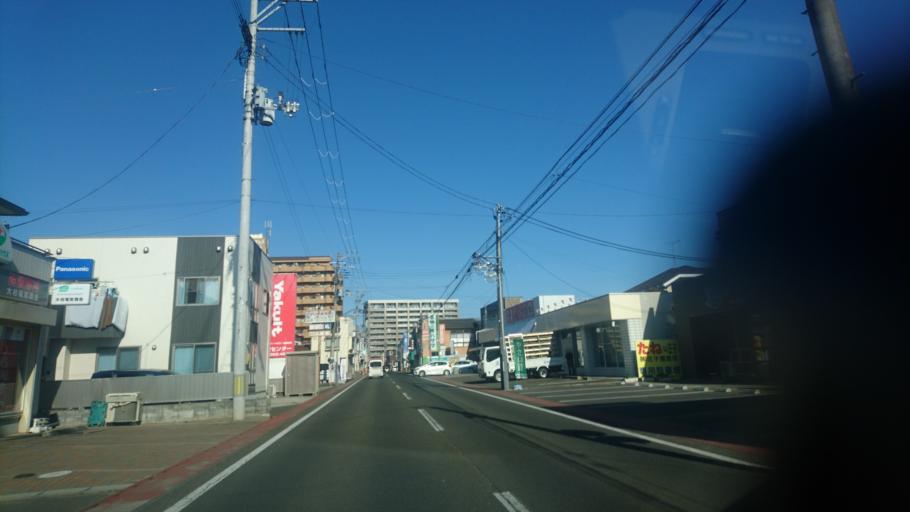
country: JP
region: Miyagi
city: Iwanuma
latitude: 38.1680
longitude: 140.8848
